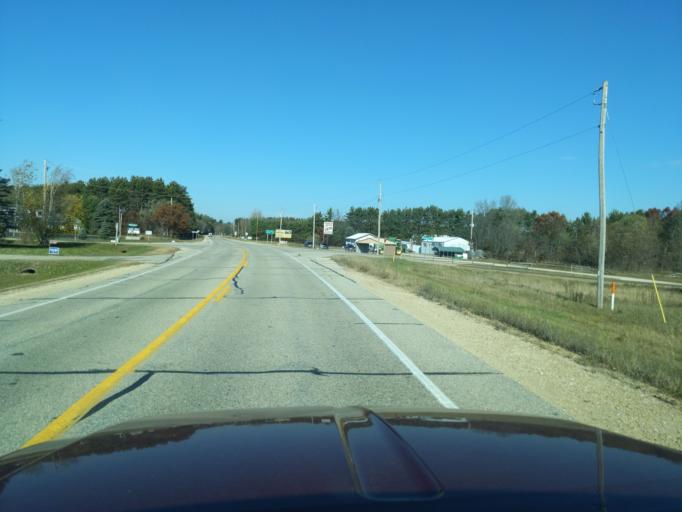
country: US
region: Wisconsin
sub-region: Waushara County
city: Wautoma
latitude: 44.0571
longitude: -89.2932
